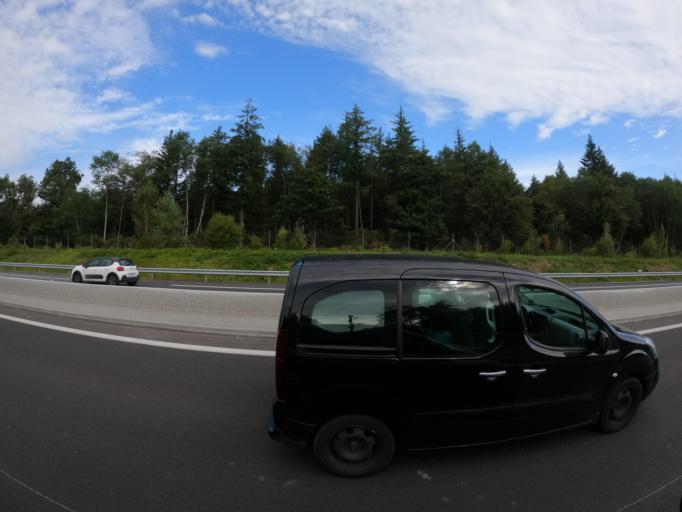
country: FR
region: Centre
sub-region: Departement d'Indre-et-Loire
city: Langeais
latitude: 47.3311
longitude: 0.3460
